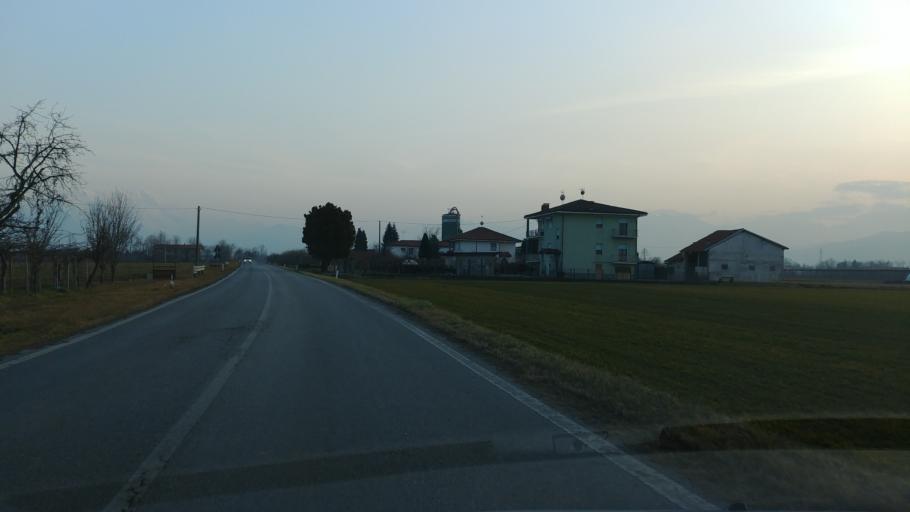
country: IT
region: Piedmont
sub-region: Provincia di Cuneo
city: Roata Rossi
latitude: 44.4241
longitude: 7.5067
